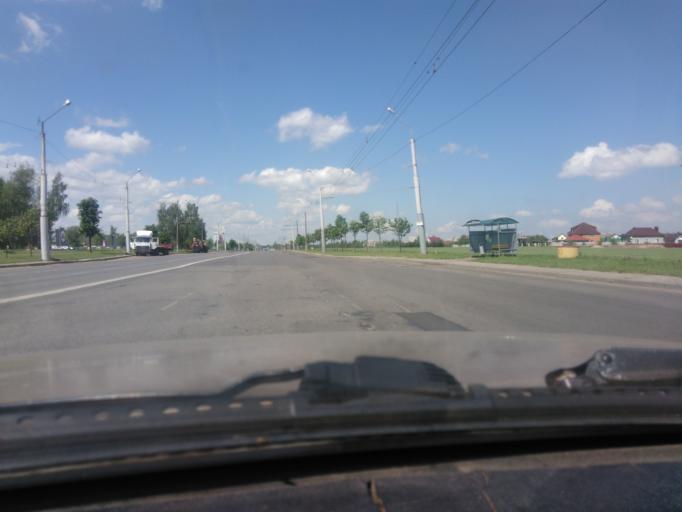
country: BY
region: Mogilev
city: Palykavichy Pyershyya
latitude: 53.9612
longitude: 30.3594
